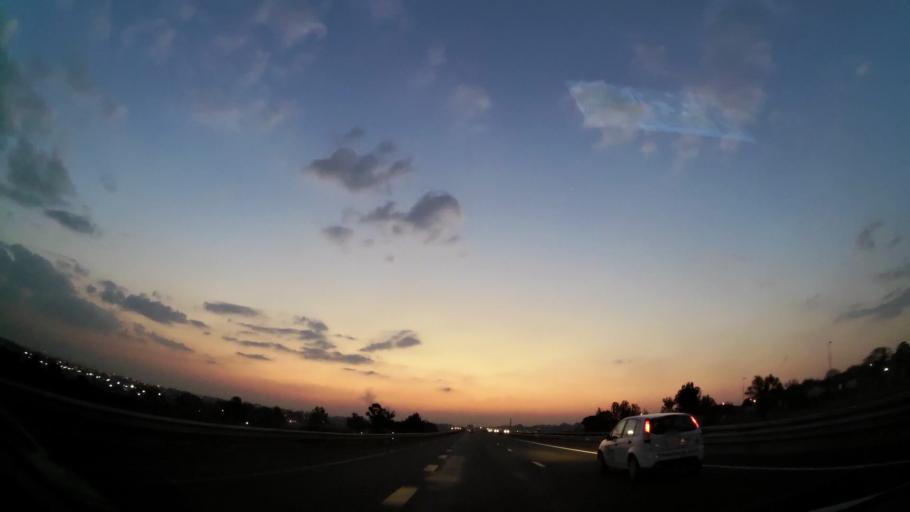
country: ZA
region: Gauteng
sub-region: Ekurhuleni Metropolitan Municipality
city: Brakpan
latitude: -26.2719
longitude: 28.3696
